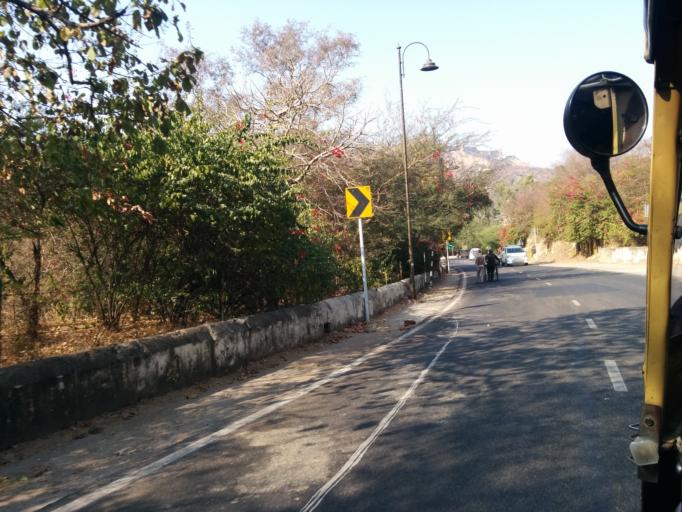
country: IN
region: Rajasthan
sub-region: Jaipur
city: Jaipur
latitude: 26.9746
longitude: 75.8518
